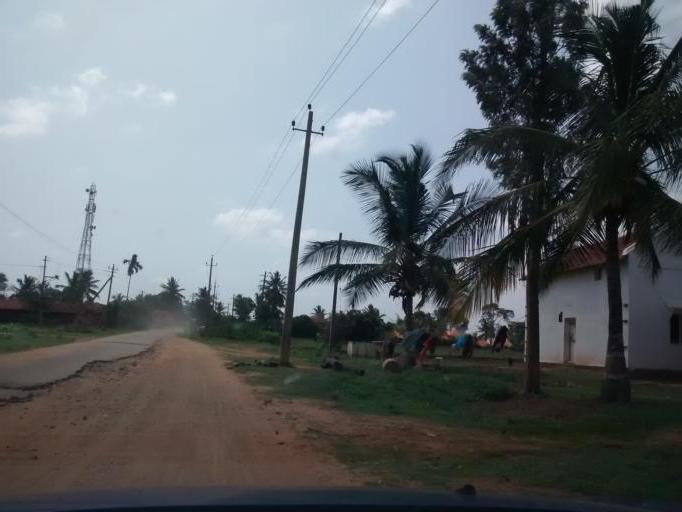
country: IN
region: Karnataka
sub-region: Hassan
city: Hole Narsipur
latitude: 12.6914
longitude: 76.1906
